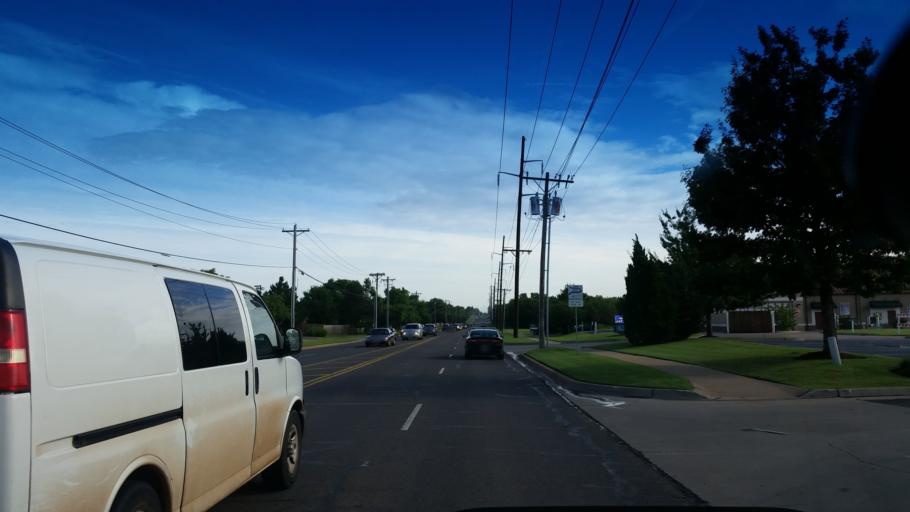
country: US
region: Oklahoma
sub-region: Oklahoma County
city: Edmond
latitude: 35.6394
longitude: -97.5138
